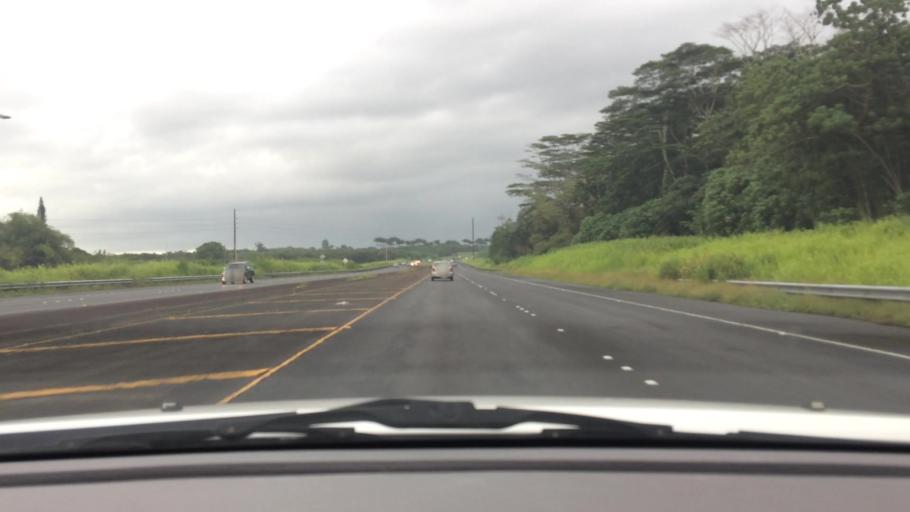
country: US
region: Hawaii
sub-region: Hawaii County
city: Kea'au
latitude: 19.6255
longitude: -155.0325
